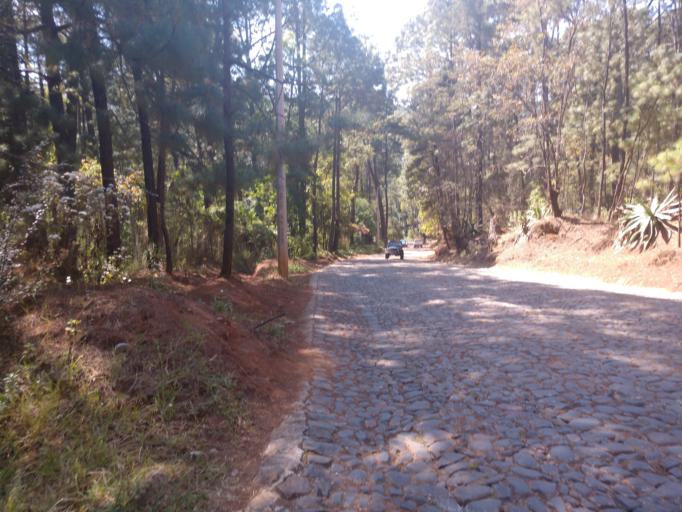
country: MX
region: Jalisco
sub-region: Mazamitla
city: Mazamitla
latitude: 19.9035
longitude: -103.0322
